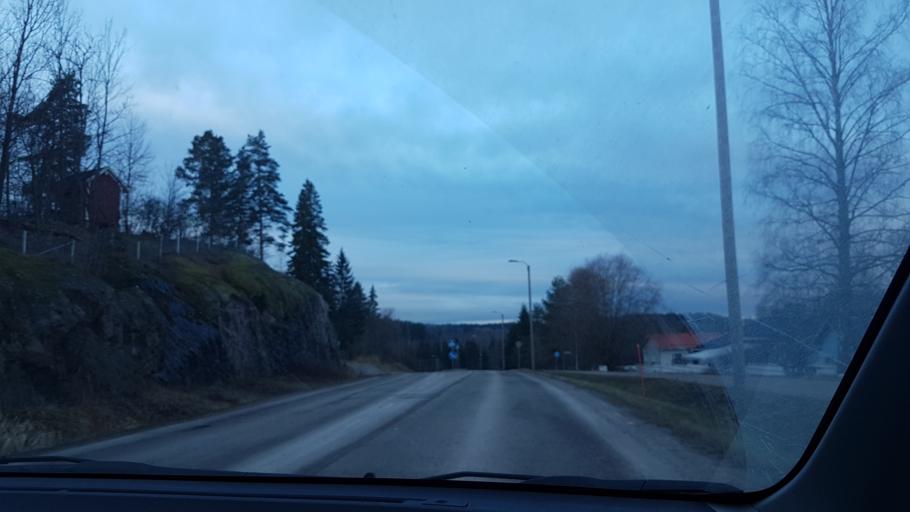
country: FI
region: Uusimaa
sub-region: Helsinki
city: Nurmijaervi
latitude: 60.3639
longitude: 24.7482
